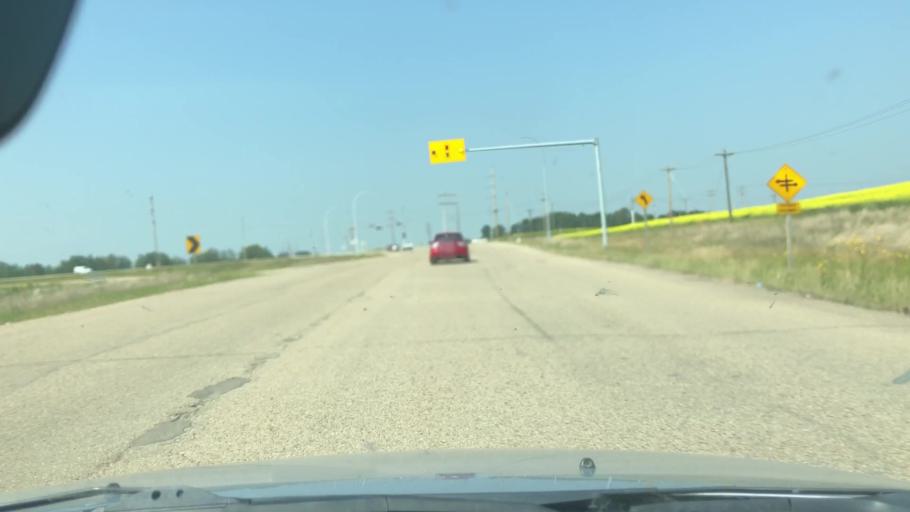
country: CA
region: Alberta
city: Devon
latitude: 53.5122
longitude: -113.7586
